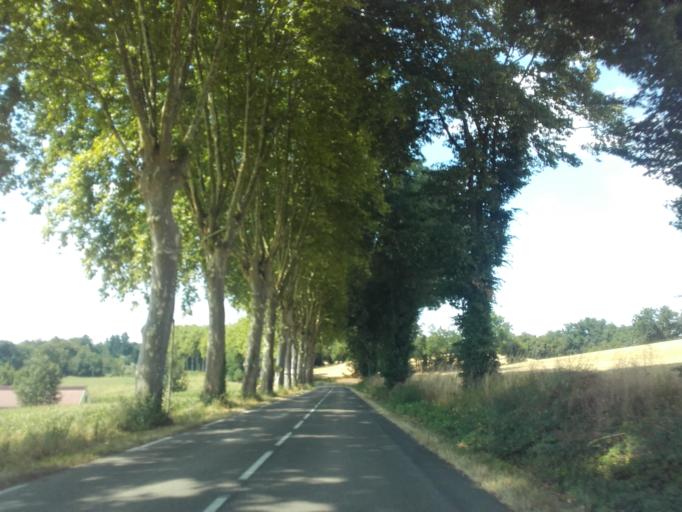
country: FR
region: Rhone-Alpes
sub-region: Departement de l'Ain
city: Chalamont
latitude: 45.9996
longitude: 5.1659
